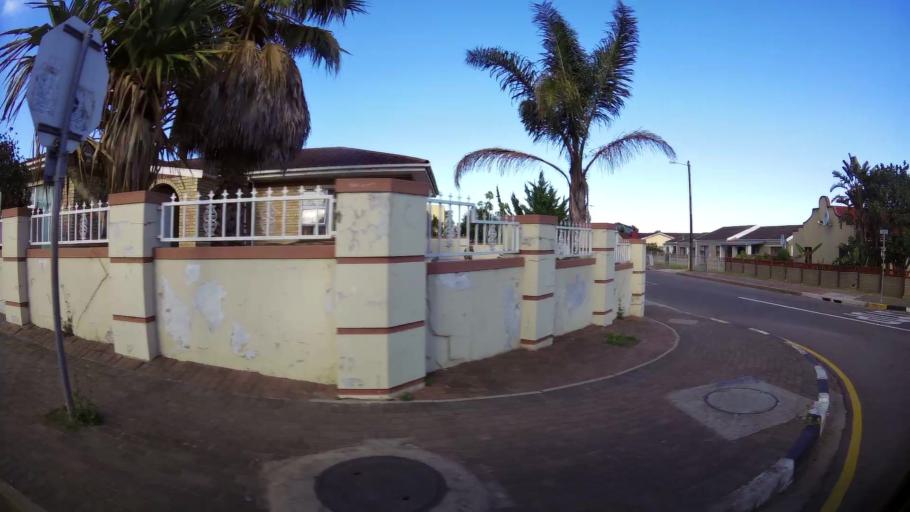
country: ZA
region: Western Cape
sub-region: Eden District Municipality
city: George
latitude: -33.9683
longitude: 22.4841
